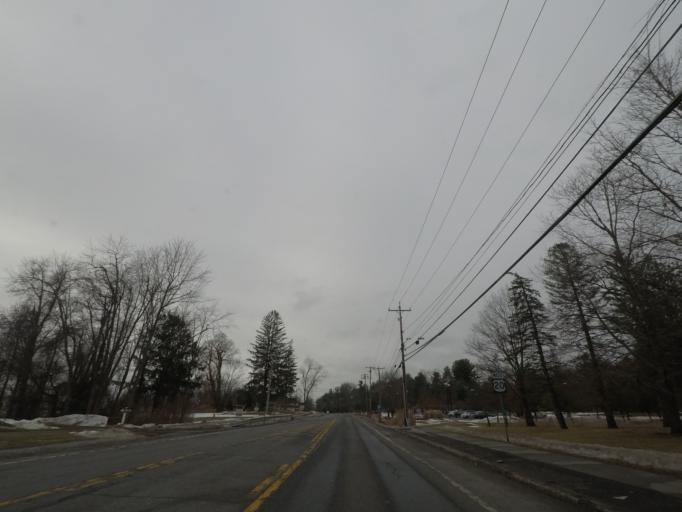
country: US
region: New York
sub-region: Albany County
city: Voorheesville
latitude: 42.7162
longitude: -73.9354
